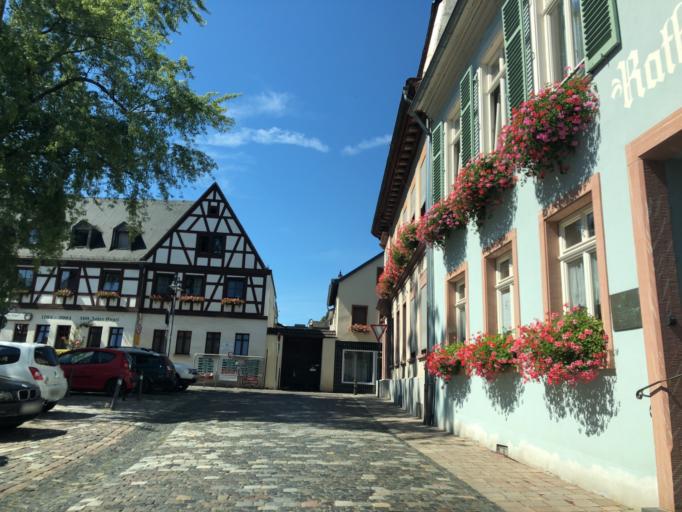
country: DE
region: Hesse
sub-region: Regierungsbezirk Darmstadt
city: Kiedrich
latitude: 50.0202
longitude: 8.0956
